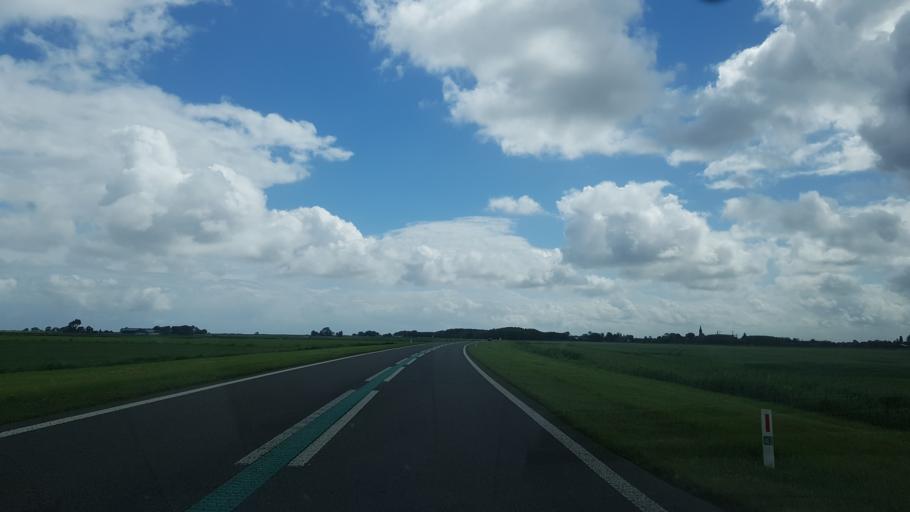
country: NL
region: Friesland
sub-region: Gemeente Dongeradeel
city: Anjum
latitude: 53.3753
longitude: 6.1023
